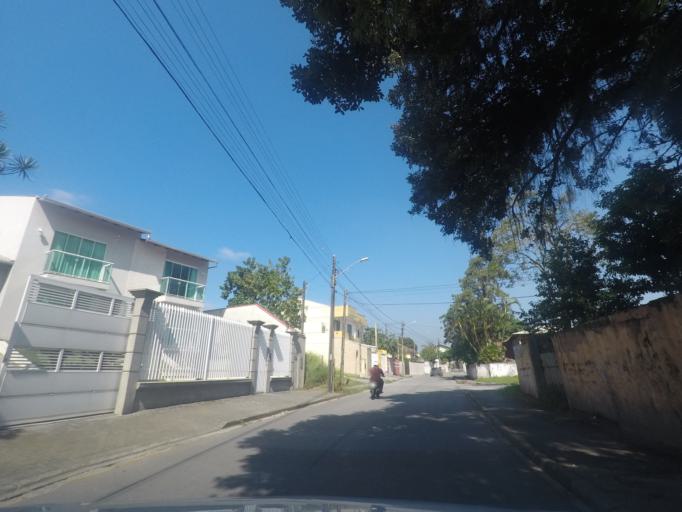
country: BR
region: Parana
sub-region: Paranagua
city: Paranagua
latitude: -25.5260
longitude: -48.5131
